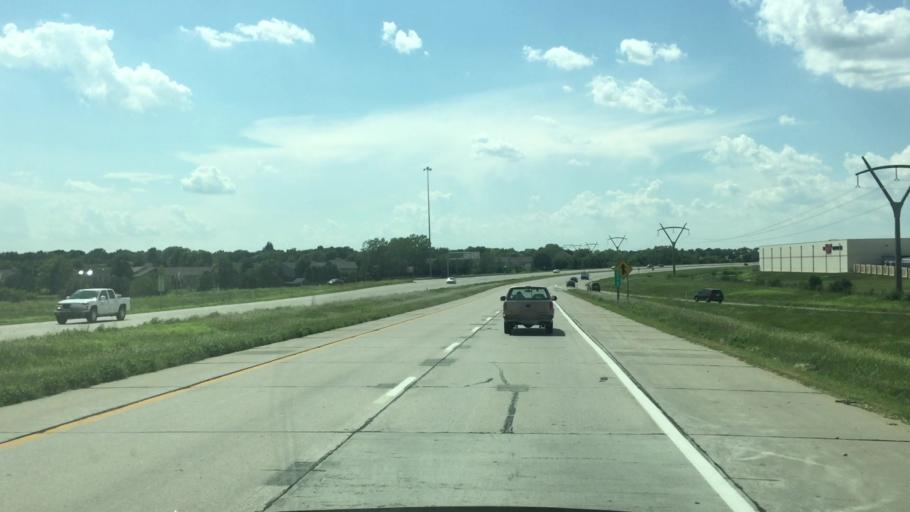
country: US
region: Kansas
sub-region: Sedgwick County
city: Bellaire
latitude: 37.7300
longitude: -97.2108
